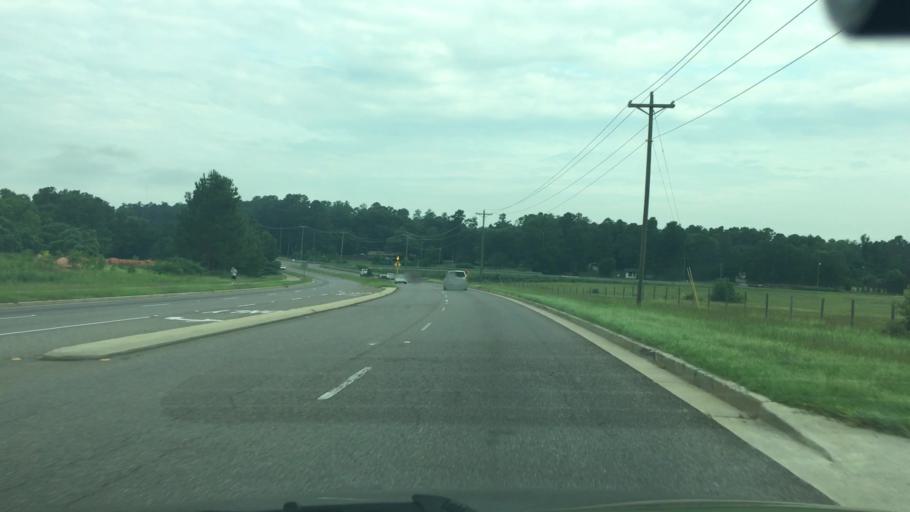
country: US
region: South Carolina
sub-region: Aiken County
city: Aiken
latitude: 33.5690
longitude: -81.6895
